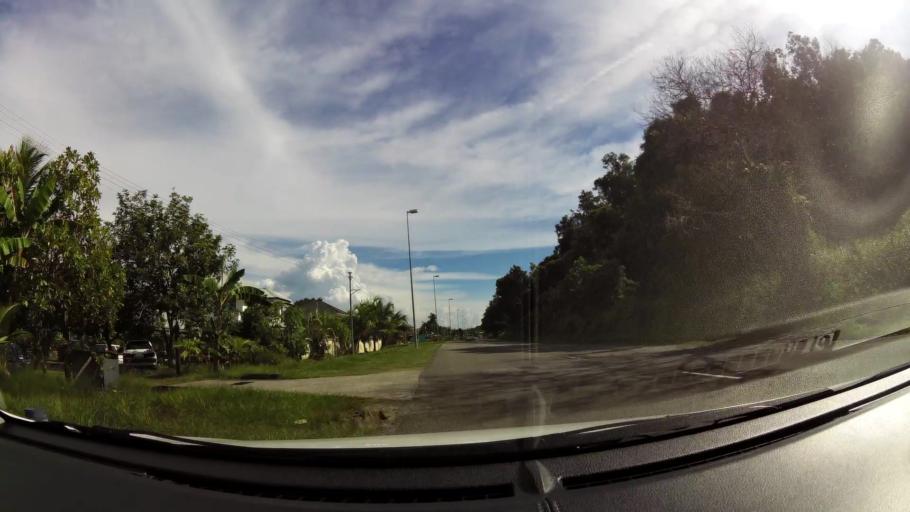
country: BN
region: Brunei and Muara
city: Bandar Seri Begawan
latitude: 5.0202
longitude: 115.0389
